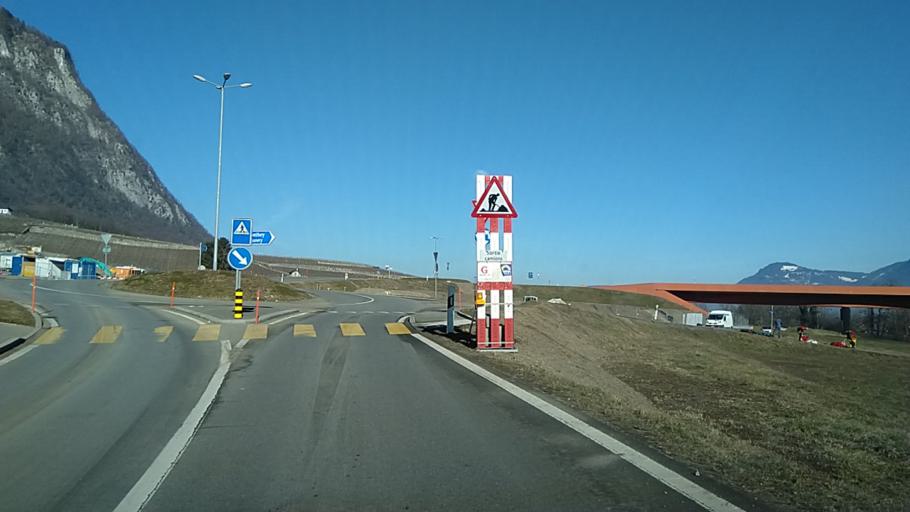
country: CH
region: Valais
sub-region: Monthey District
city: Port-Valais
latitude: 46.3564
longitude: 6.8788
